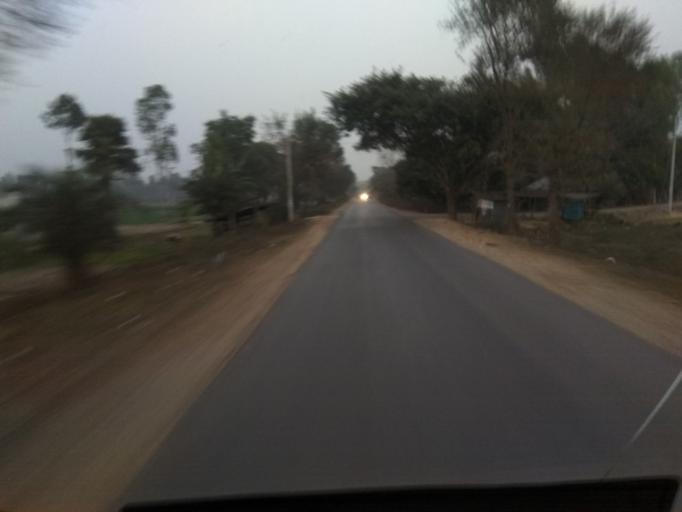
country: BD
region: Rajshahi
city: Bogra
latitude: 24.7462
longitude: 89.3385
